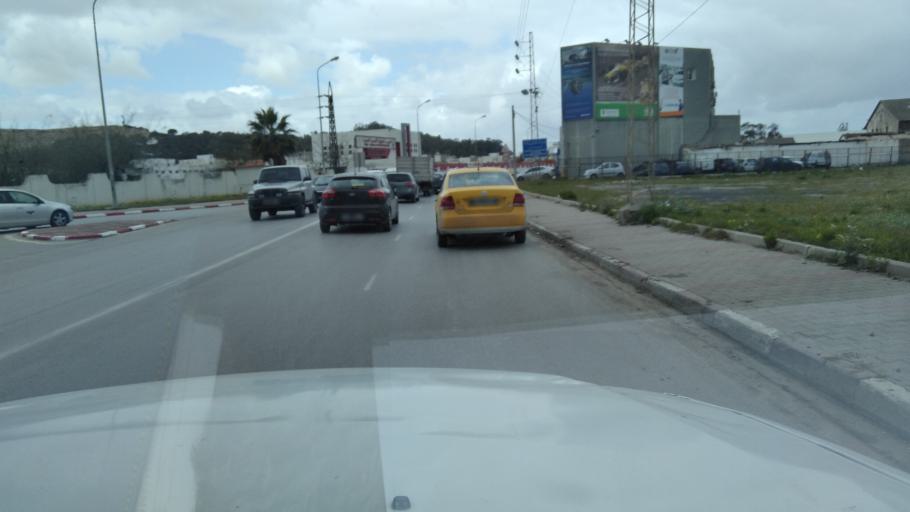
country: TN
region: Bin 'Arus
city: Ben Arous
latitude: 36.7595
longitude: 10.2163
